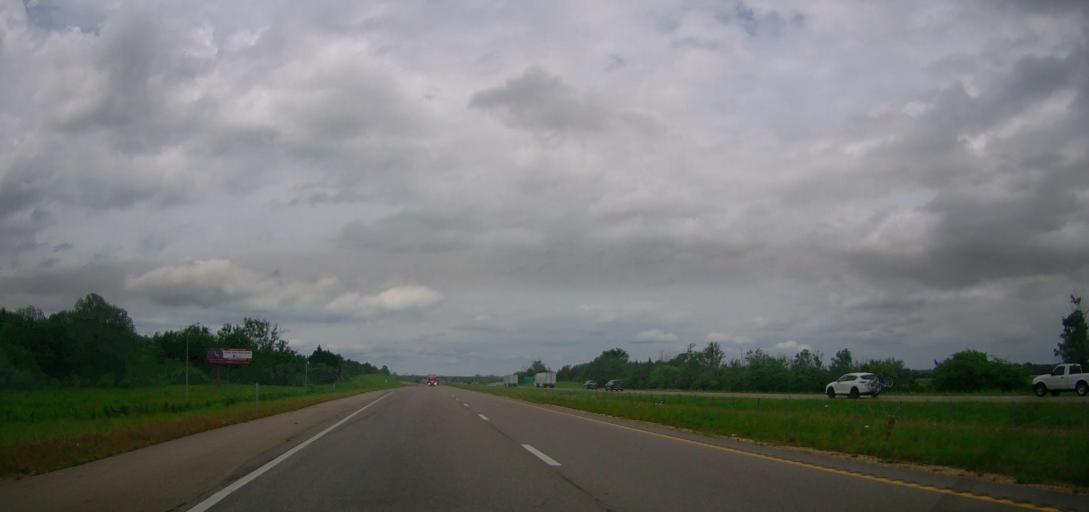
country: US
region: Mississippi
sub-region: Lee County
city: Tupelo
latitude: 34.3035
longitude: -88.7617
